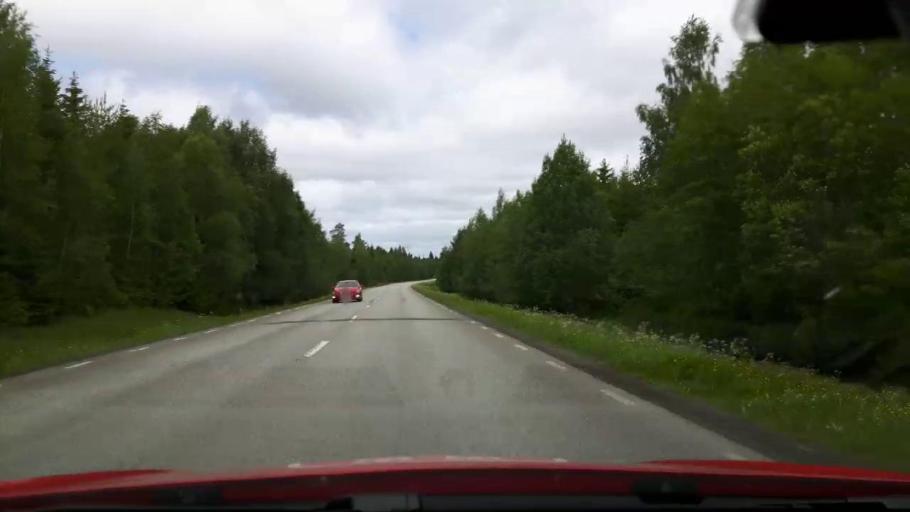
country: SE
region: Jaemtland
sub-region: Krokoms Kommun
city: Krokom
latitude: 63.3730
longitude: 14.5067
